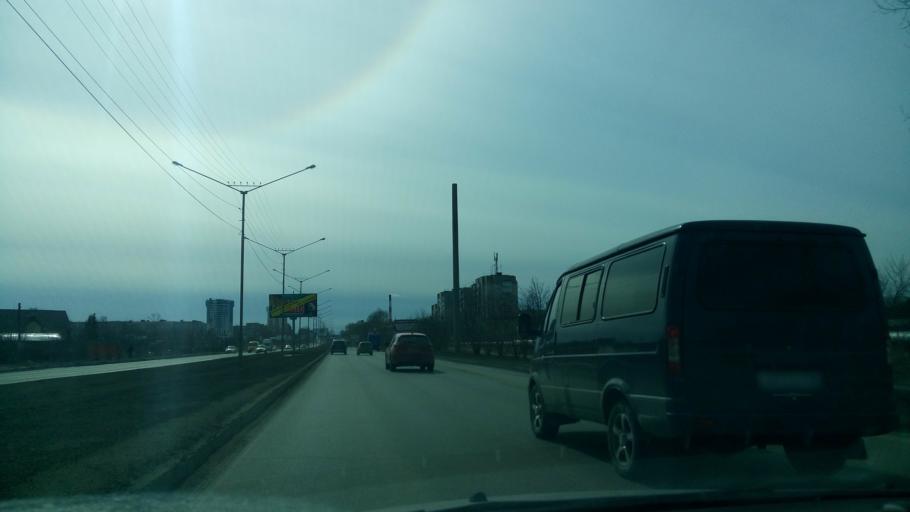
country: RU
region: Sverdlovsk
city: Nizhniy Tagil
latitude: 57.8918
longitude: 59.9408
